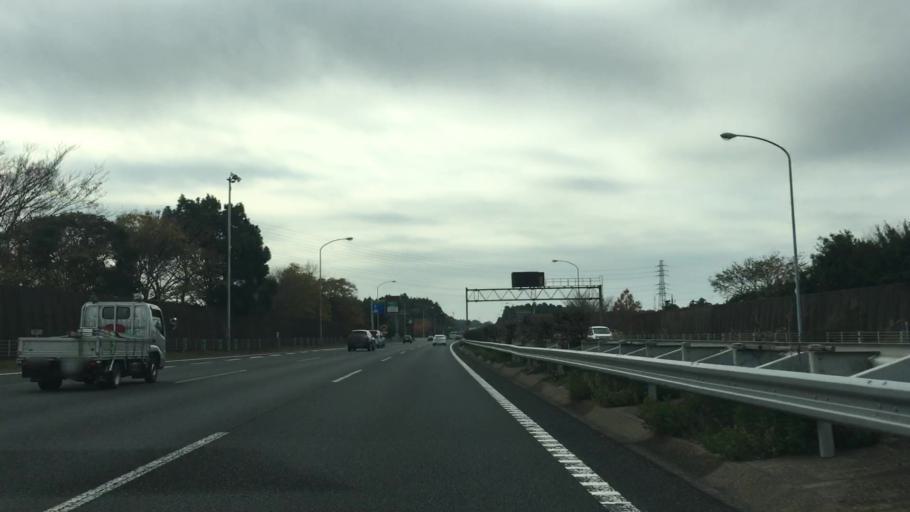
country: JP
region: Chiba
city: Narita
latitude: 35.7410
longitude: 140.3081
